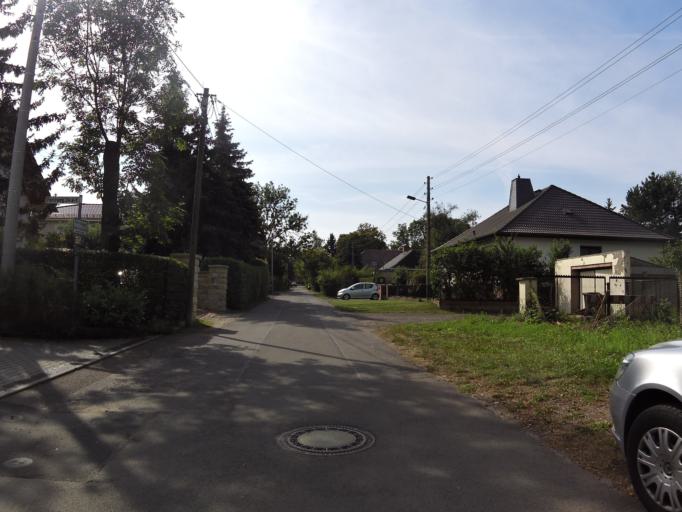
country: DE
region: Saxony
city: Schkeuditz
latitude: 51.3628
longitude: 12.2805
